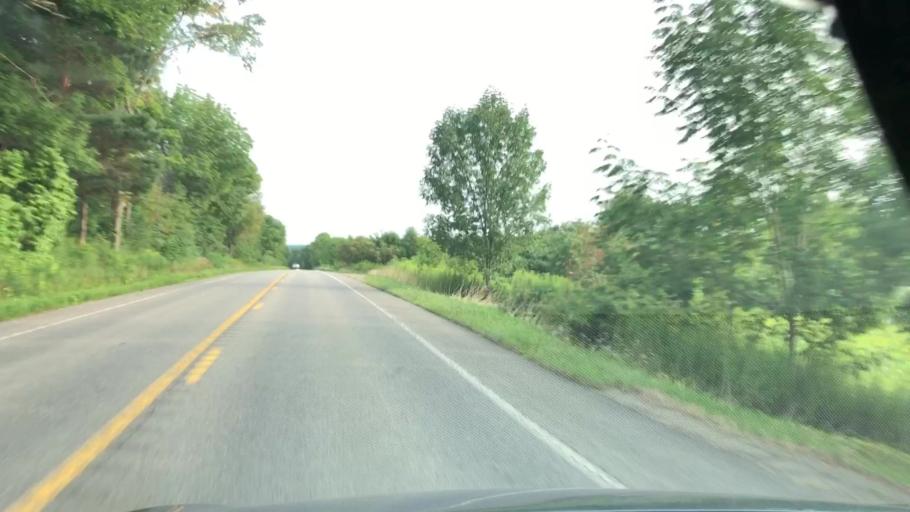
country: US
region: Pennsylvania
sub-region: Erie County
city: Union City
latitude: 41.8435
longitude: -79.8222
